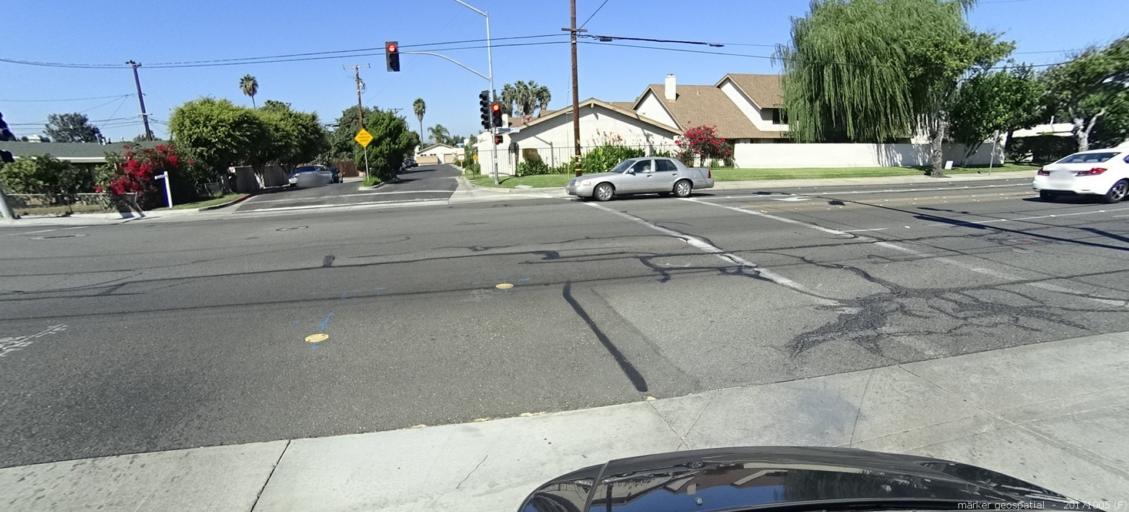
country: US
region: California
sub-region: Orange County
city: Garden Grove
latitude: 33.7885
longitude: -117.9499
